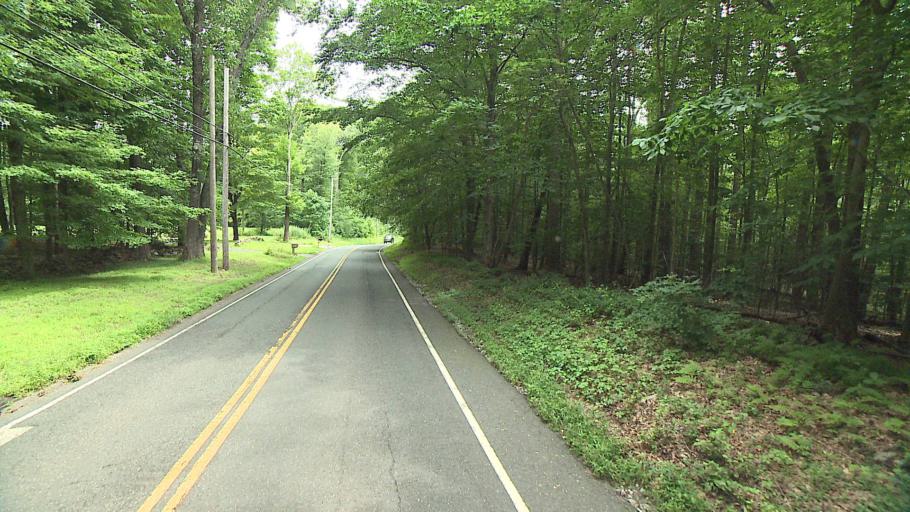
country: US
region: Connecticut
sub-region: Litchfield County
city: Woodbury
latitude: 41.5525
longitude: -73.2462
